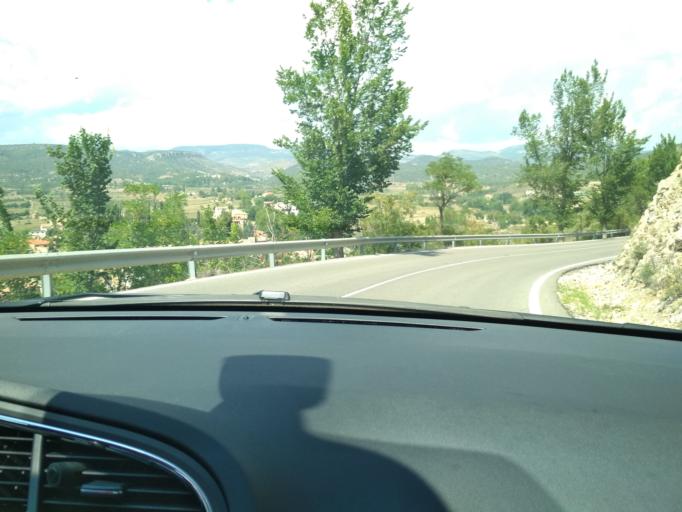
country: ES
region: Aragon
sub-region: Provincia de Teruel
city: Rubielos de Mora
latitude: 40.1885
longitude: -0.6499
